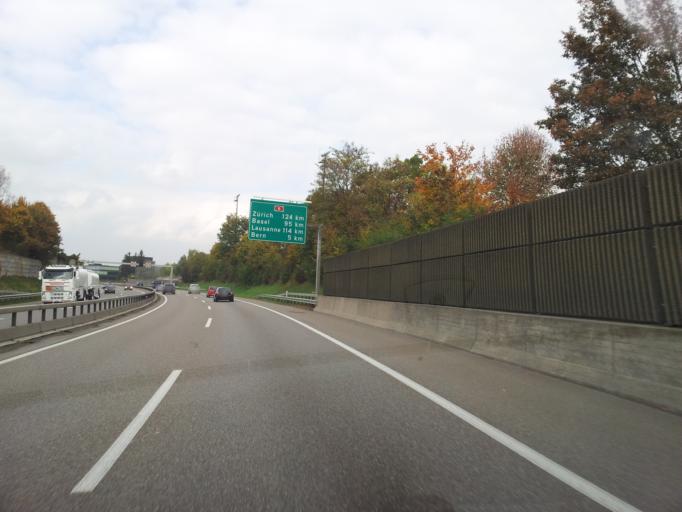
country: CH
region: Bern
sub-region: Bern-Mittelland District
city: Muri
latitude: 46.9321
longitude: 7.4997
